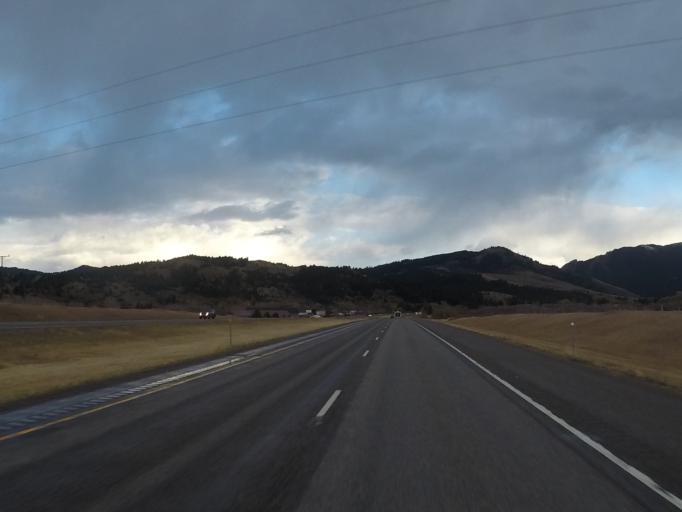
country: US
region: Montana
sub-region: Gallatin County
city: Bozeman
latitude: 45.6627
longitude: -110.9635
